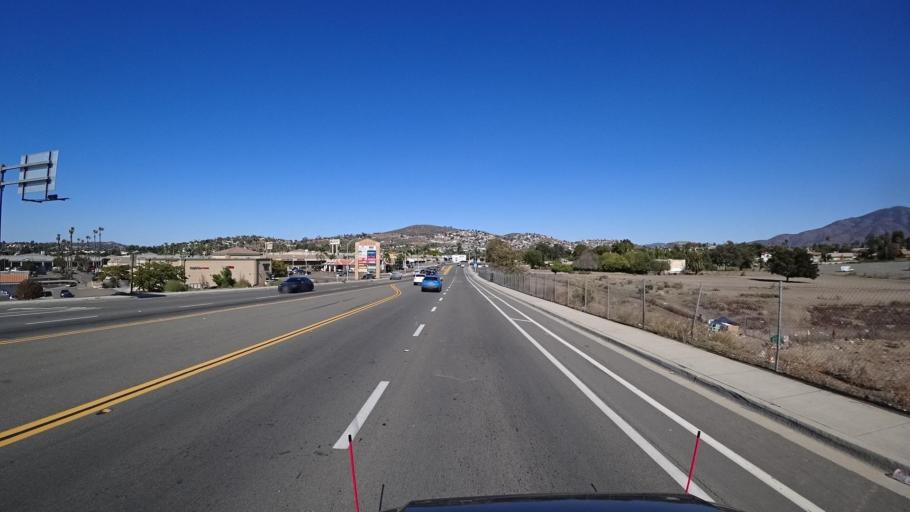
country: US
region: California
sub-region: San Diego County
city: La Presa
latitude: 32.7056
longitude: -117.0097
